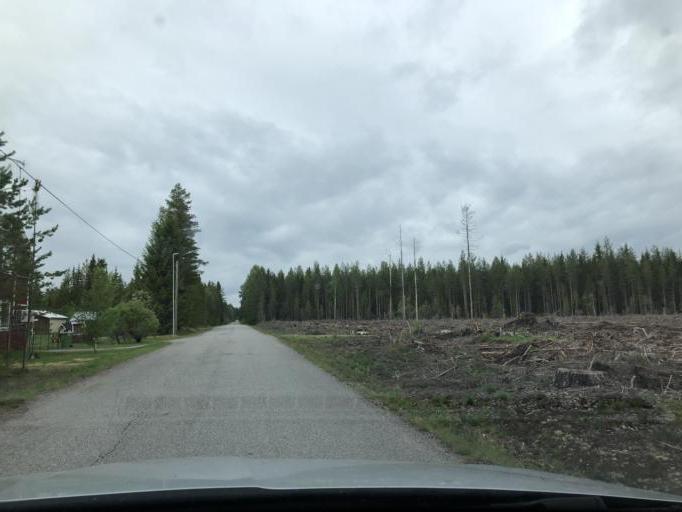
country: SE
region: Norrbotten
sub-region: Pitea Kommun
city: Roknas
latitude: 65.3787
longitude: 21.2768
